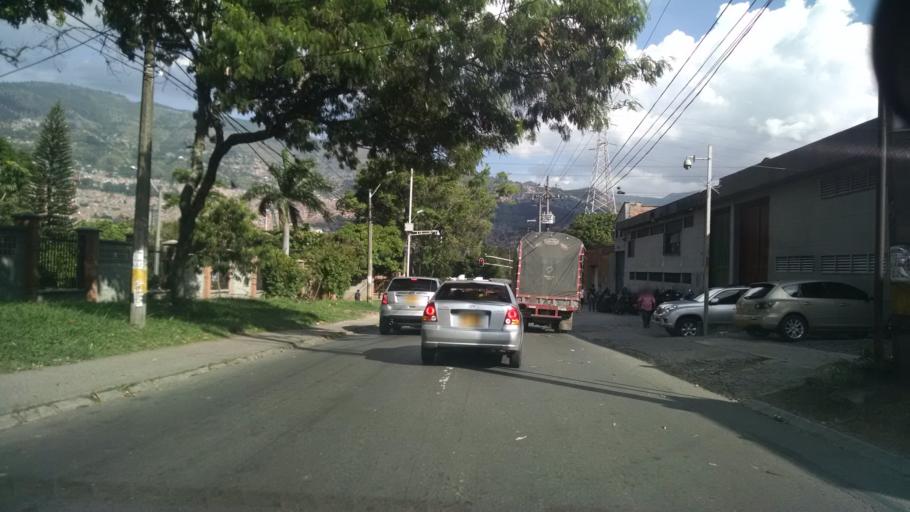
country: CO
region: Antioquia
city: Medellin
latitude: 6.2769
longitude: -75.5744
